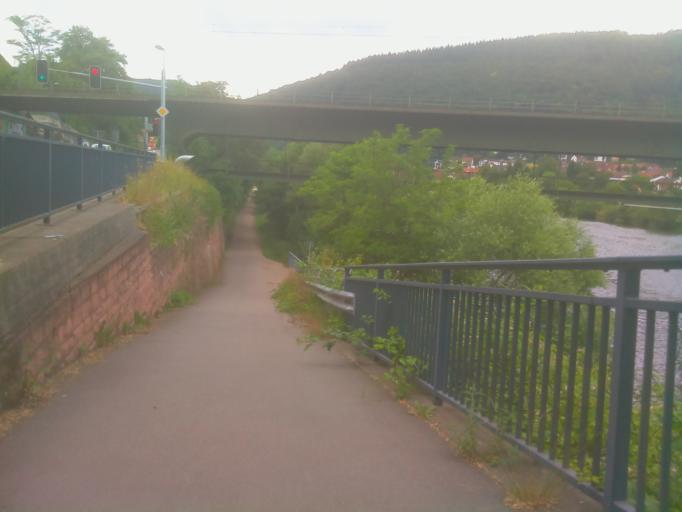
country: DE
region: Baden-Wuerttemberg
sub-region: Karlsruhe Region
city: Neckargemund
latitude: 49.3924
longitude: 8.8059
